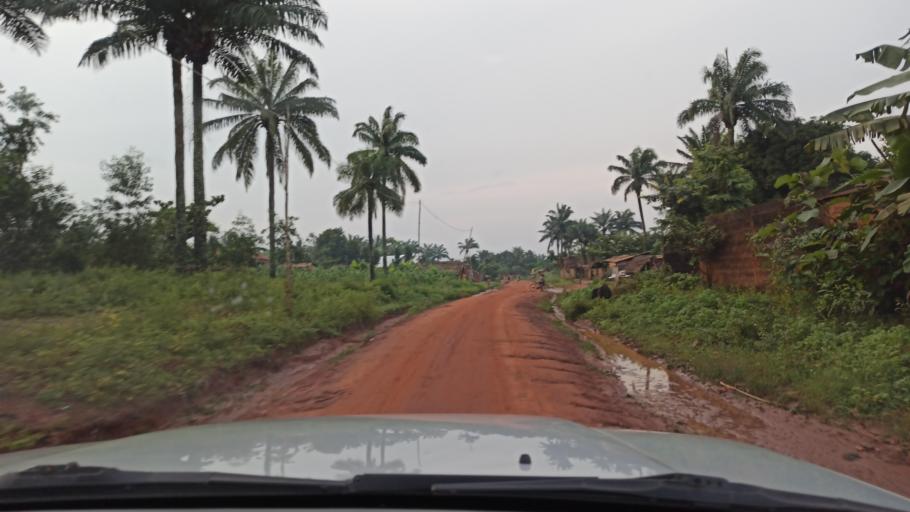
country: BJ
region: Queme
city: Porto-Novo
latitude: 6.5432
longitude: 2.6199
